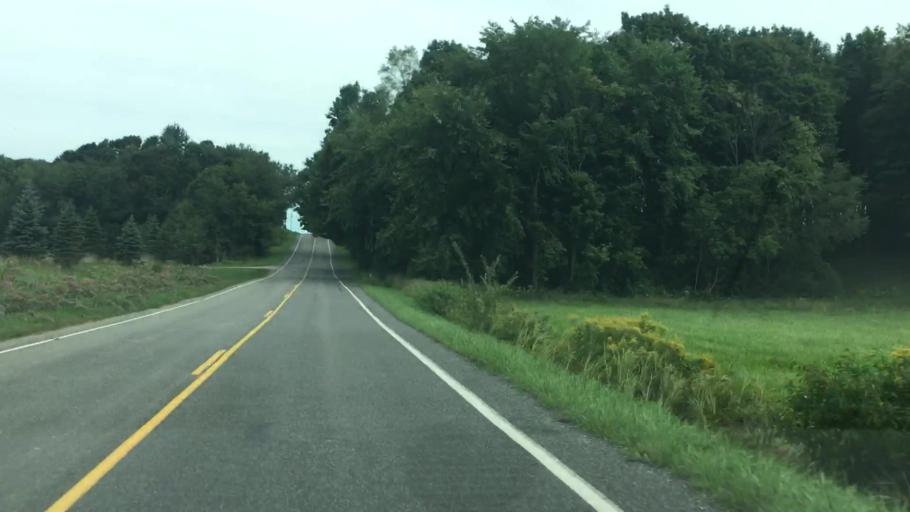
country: US
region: Michigan
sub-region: Kent County
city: Byron Center
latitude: 42.8290
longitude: -85.7827
